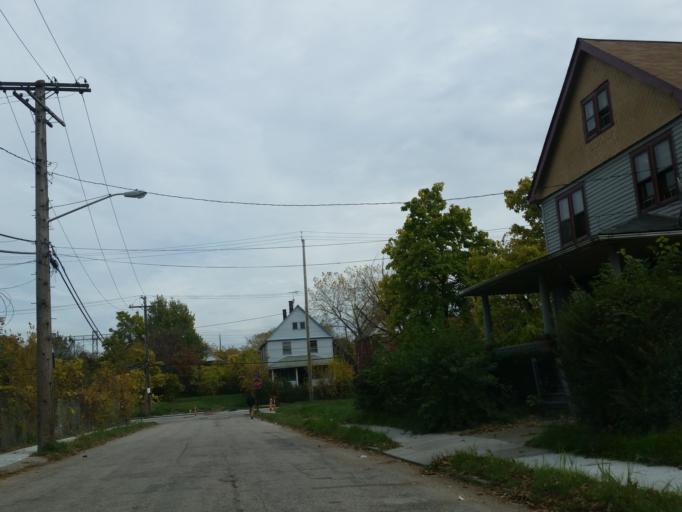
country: US
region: Ohio
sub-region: Cuyahoga County
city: Newburgh Heights
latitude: 41.4776
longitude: -81.6320
